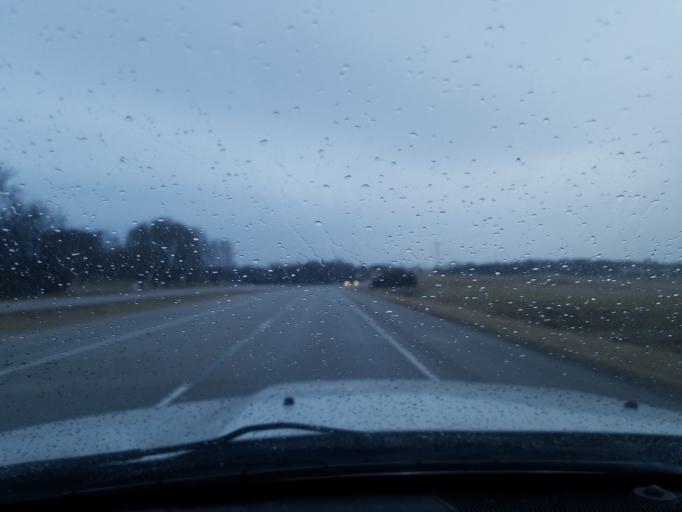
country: US
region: Kentucky
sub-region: Logan County
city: Auburn
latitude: 36.9061
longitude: -86.5863
